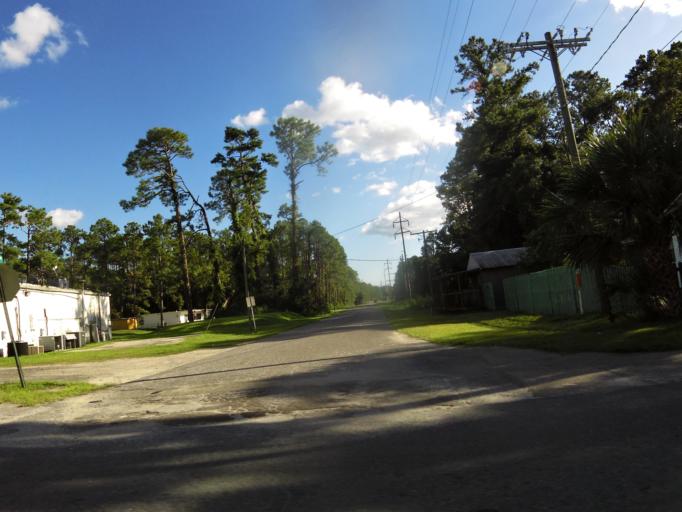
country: US
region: Florida
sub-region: Wakulla County
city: Crawfordville
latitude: 30.0610
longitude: -84.4901
